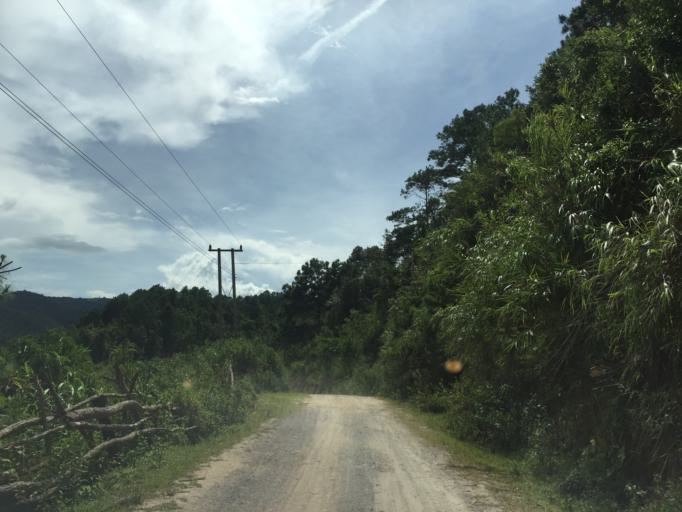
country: LA
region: Xiangkhoang
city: Muang Phonsavan
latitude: 19.3379
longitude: 103.5231
